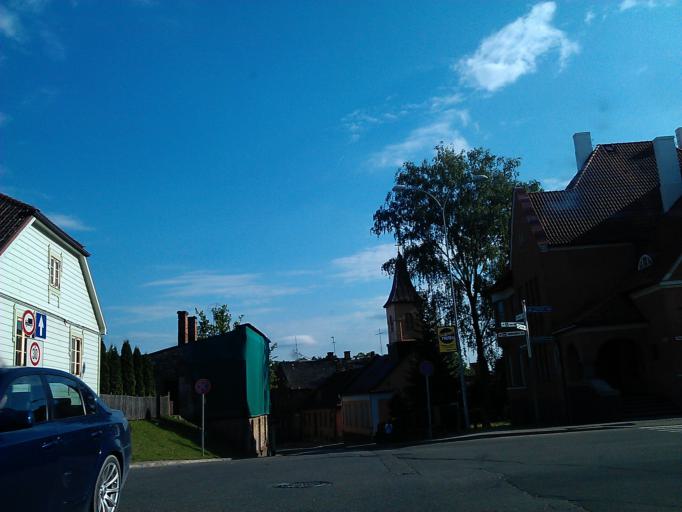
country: LV
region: Cesu Rajons
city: Cesis
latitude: 57.3121
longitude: 25.2661
